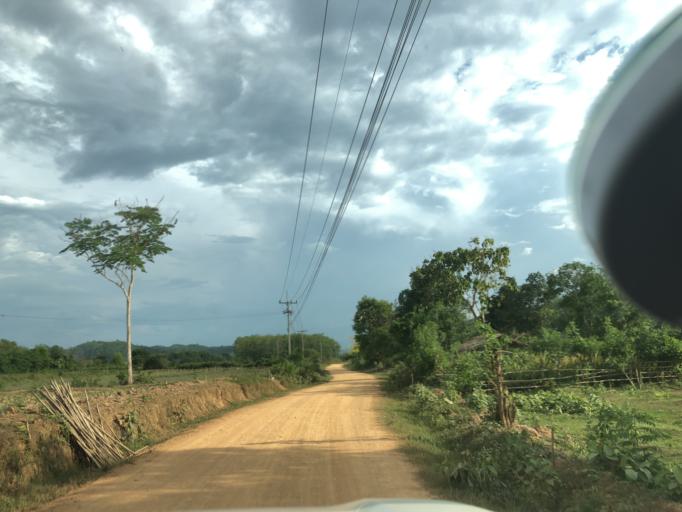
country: TH
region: Loei
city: Chiang Khan
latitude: 18.0061
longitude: 101.4206
